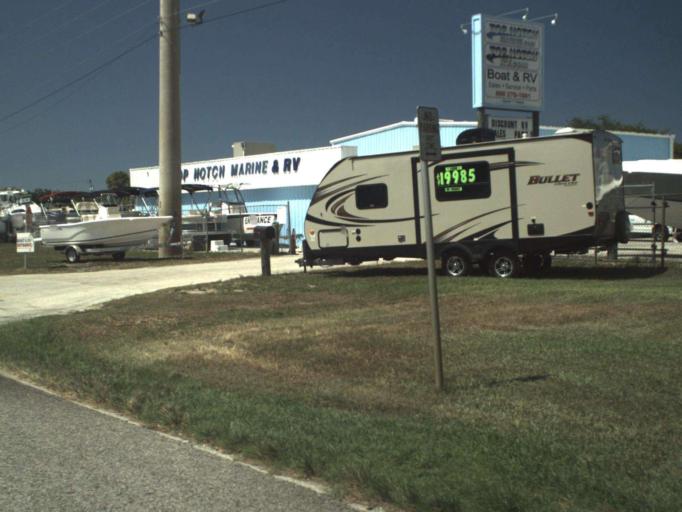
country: US
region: Florida
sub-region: Saint Lucie County
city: Fort Pierce North
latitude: 27.4796
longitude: -80.3390
